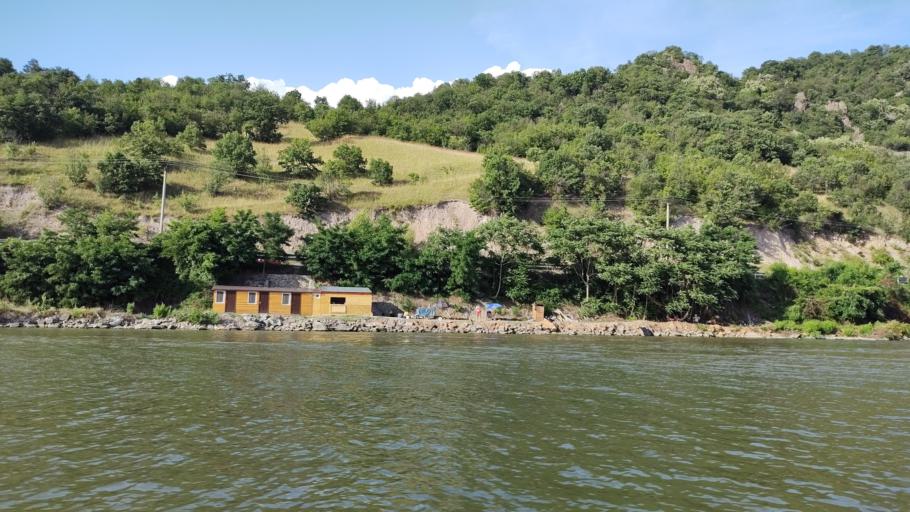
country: RO
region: Mehedinti
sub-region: Comuna Svinita
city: Svinita
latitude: 44.5482
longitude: 22.0383
